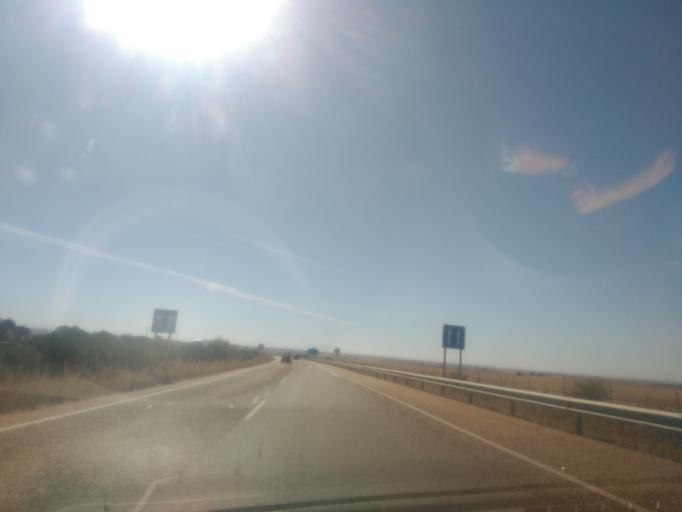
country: ES
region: Castille and Leon
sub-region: Provincia de Salamanca
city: Aldeanueva de Figueroa
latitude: 41.1316
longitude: -5.4897
